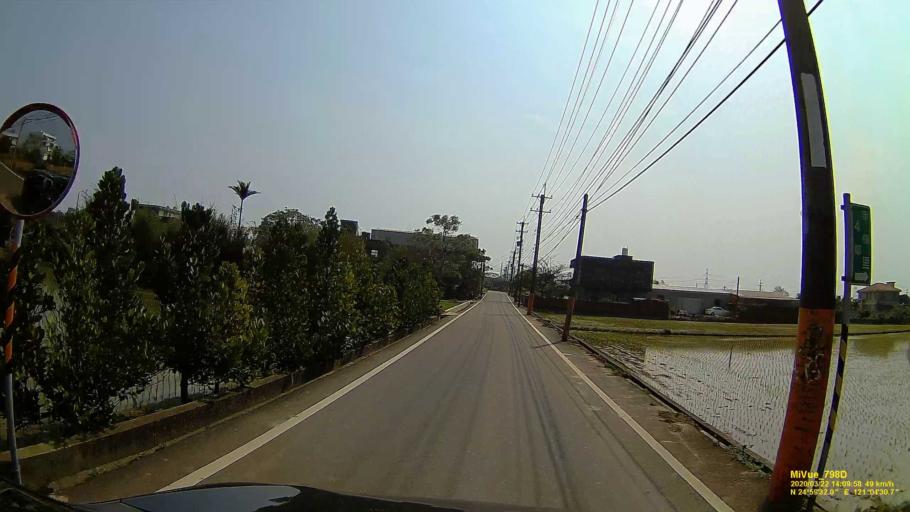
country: TW
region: Taiwan
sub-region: Hsinchu
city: Zhubei
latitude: 24.9933
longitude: 121.0760
